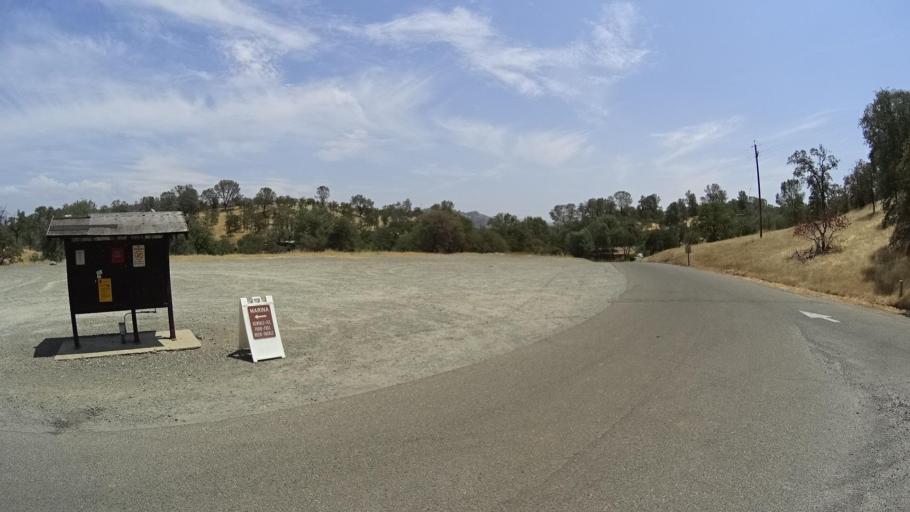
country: US
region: California
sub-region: Tuolumne County
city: Tuolumne City
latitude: 37.6452
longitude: -120.2954
